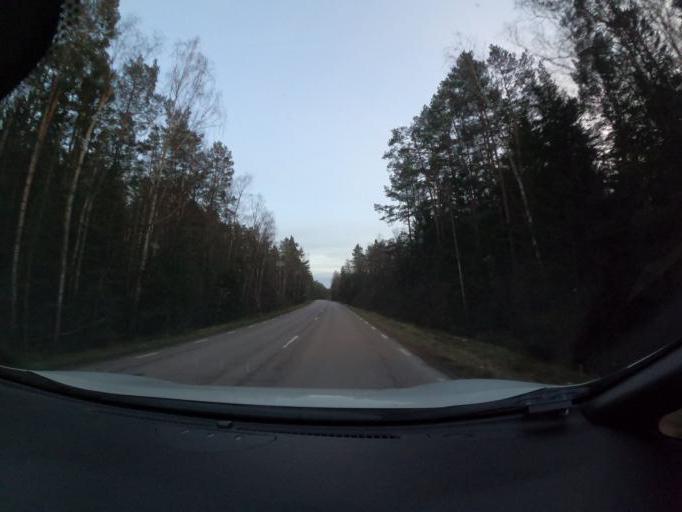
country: SE
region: Vaestra Goetaland
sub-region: Harryda Kommun
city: Molnlycke
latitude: 57.6132
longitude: 12.1790
